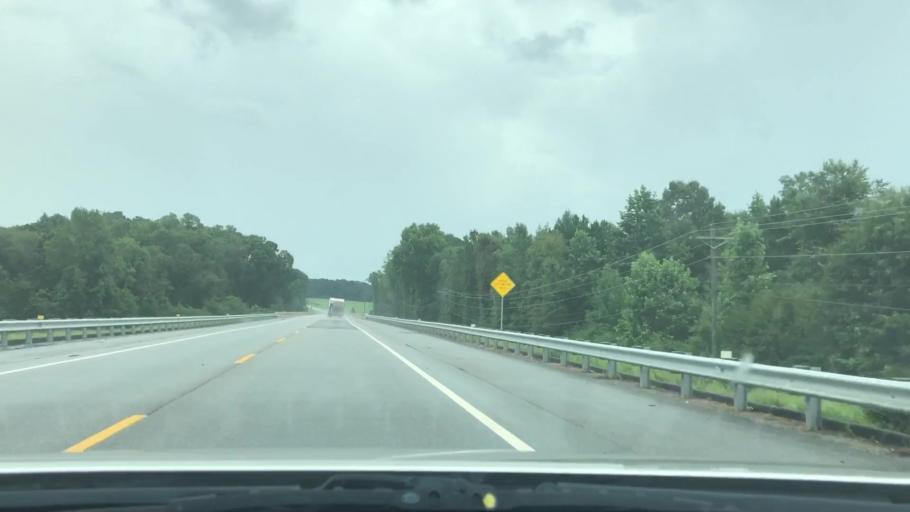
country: US
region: Georgia
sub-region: Lamar County
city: Barnesville
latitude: 33.0687
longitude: -84.2327
